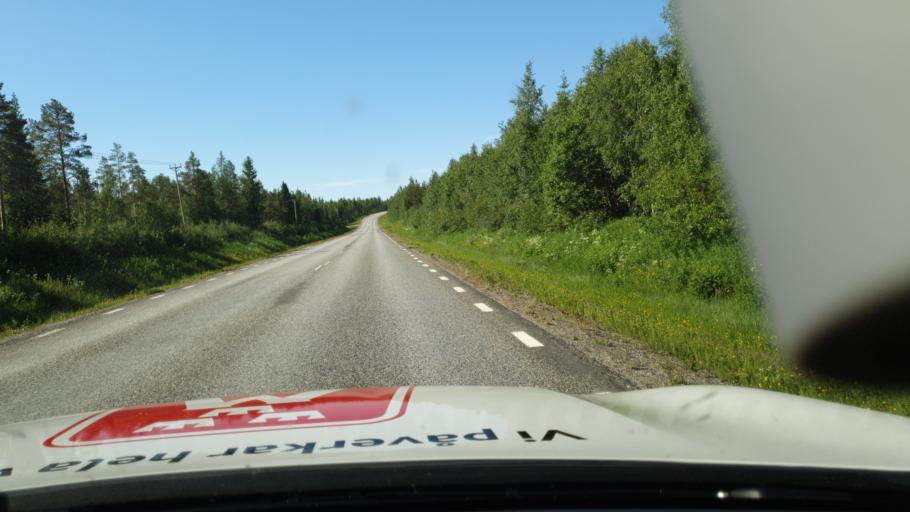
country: SE
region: Vaesterbotten
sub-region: Lycksele Kommun
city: Lycksele
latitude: 64.5477
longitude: 18.5070
